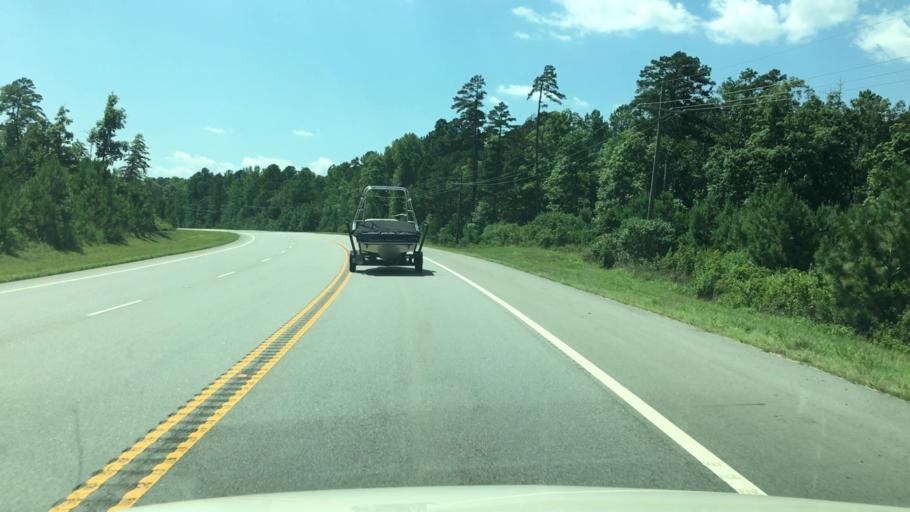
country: US
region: Arkansas
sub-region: Garland County
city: Piney
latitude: 34.5225
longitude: -93.3191
